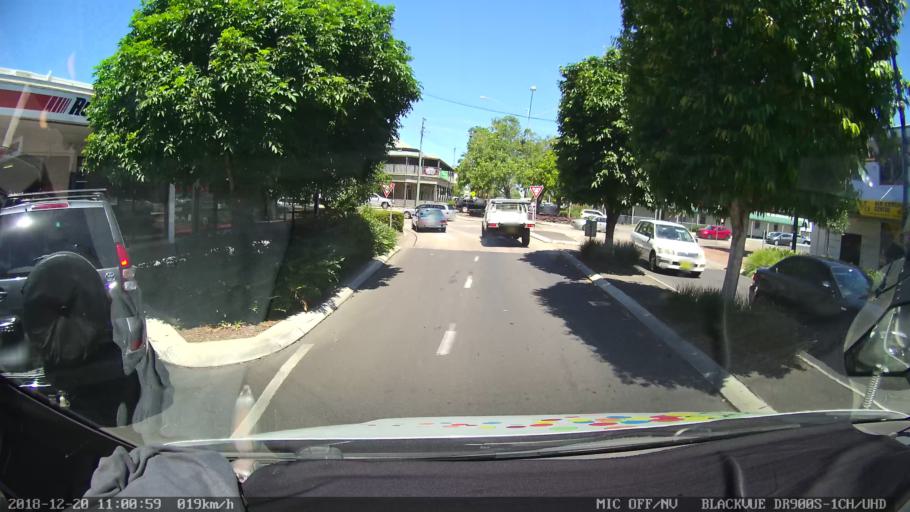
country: AU
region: New South Wales
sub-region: Richmond Valley
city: Casino
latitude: -28.8647
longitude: 153.0461
